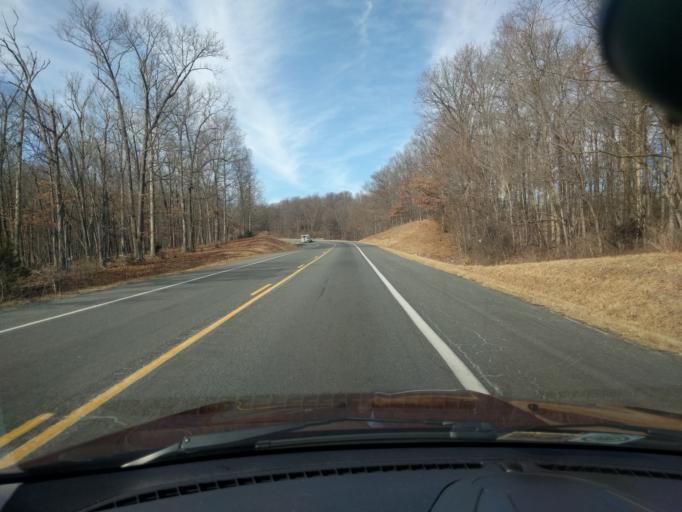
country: US
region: Virginia
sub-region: Augusta County
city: Verona
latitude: 38.1861
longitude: -79.0387
